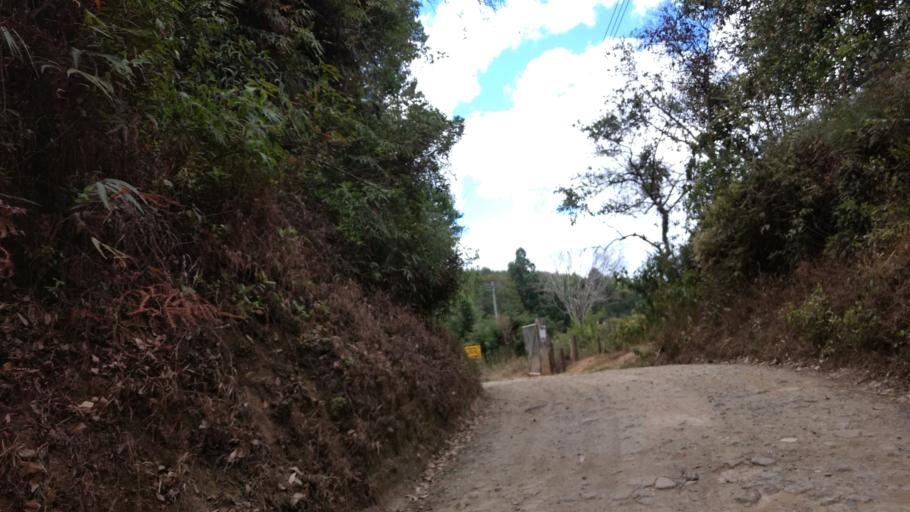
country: CO
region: Cauca
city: Popayan
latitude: 2.4634
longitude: -76.5754
